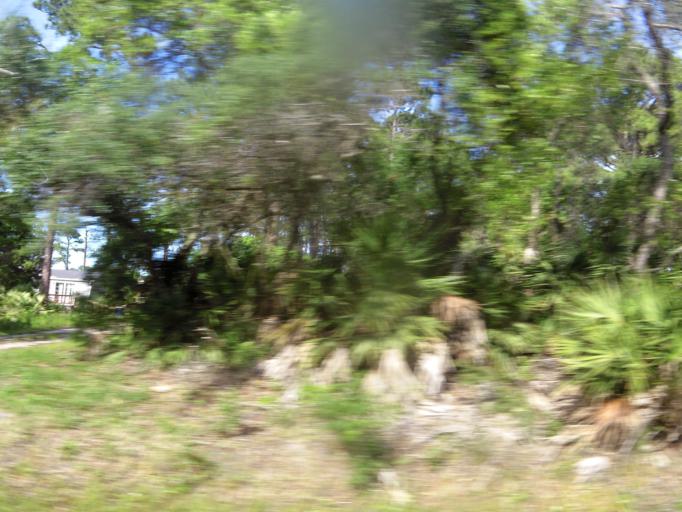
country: US
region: Florida
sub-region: Nassau County
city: Fernandina Beach
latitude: 30.5152
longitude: -81.4781
